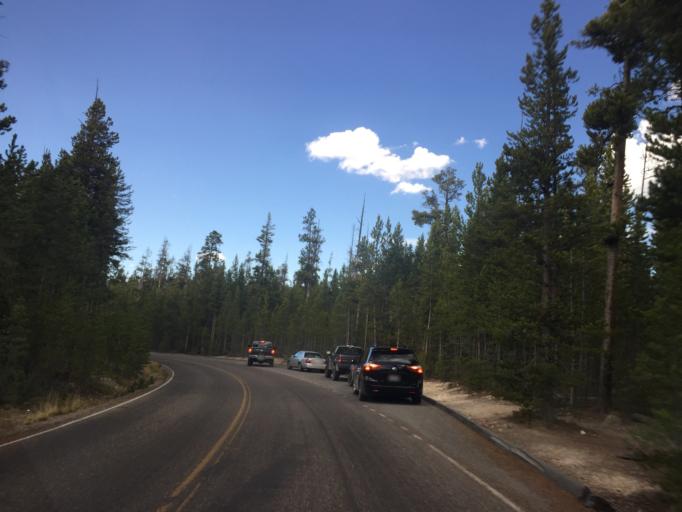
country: US
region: Montana
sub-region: Gallatin County
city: West Yellowstone
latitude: 44.7294
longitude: -110.4727
